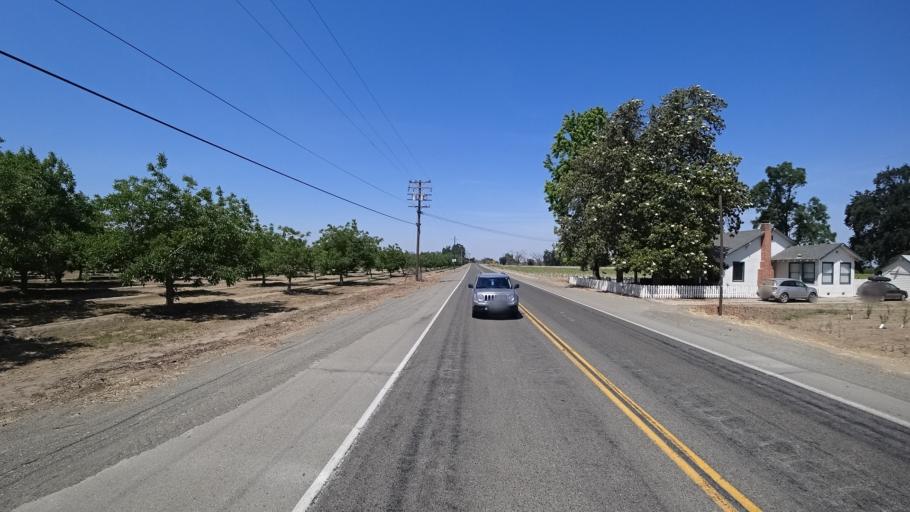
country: US
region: California
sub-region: Fresno County
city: Laton
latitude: 36.4010
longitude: -119.7455
